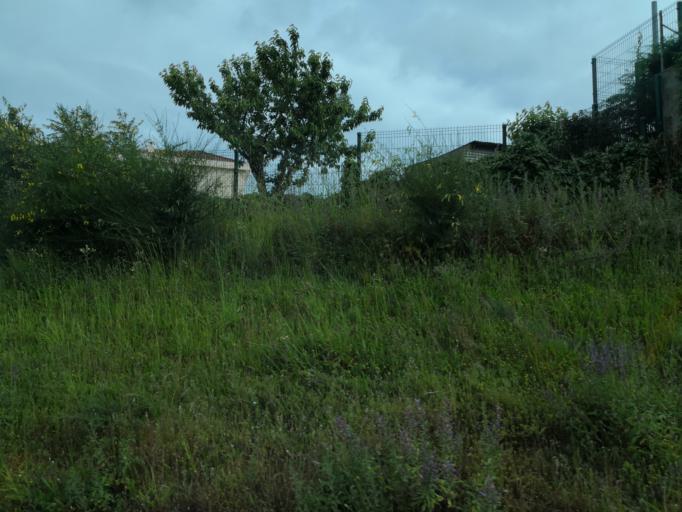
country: PT
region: Porto
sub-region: Gondomar
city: Rio Tinto
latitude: 41.1690
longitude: -8.5726
